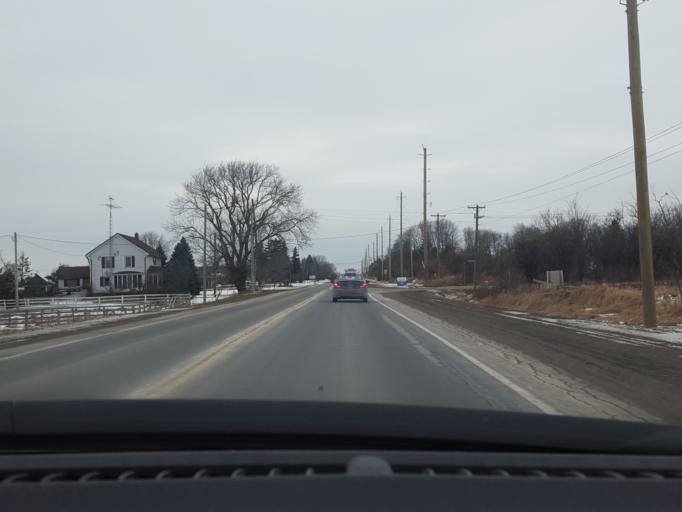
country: CA
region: Ontario
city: Keswick
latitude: 44.1631
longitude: -79.4308
